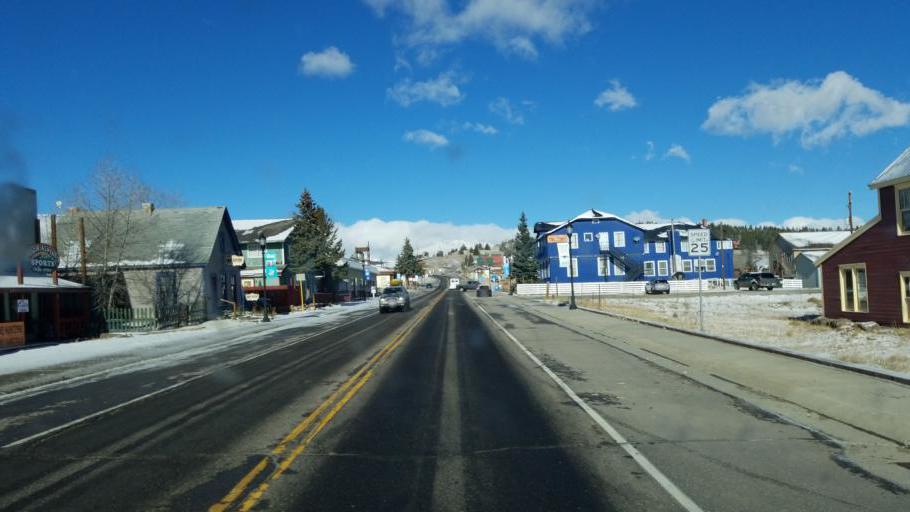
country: US
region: Colorado
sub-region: Park County
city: Fairplay
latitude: 39.2239
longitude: -106.0006
